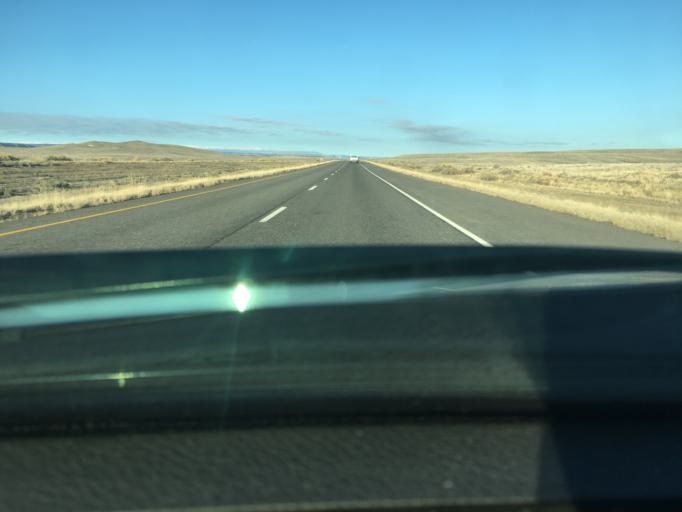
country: US
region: Colorado
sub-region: Delta County
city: Delta
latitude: 38.7650
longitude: -108.2111
